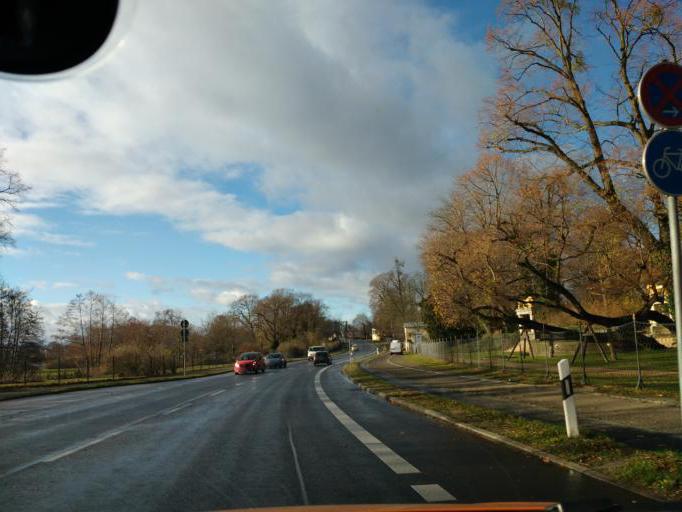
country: DE
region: Brandenburg
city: Potsdam
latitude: 52.4132
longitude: 13.0963
